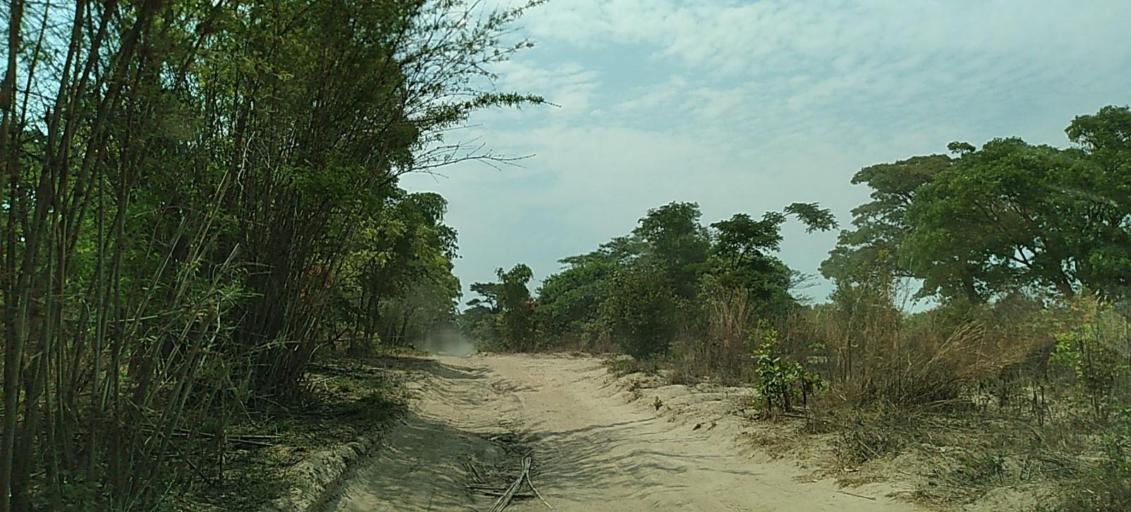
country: ZM
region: Copperbelt
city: Kalulushi
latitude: -12.9299
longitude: 28.1086
